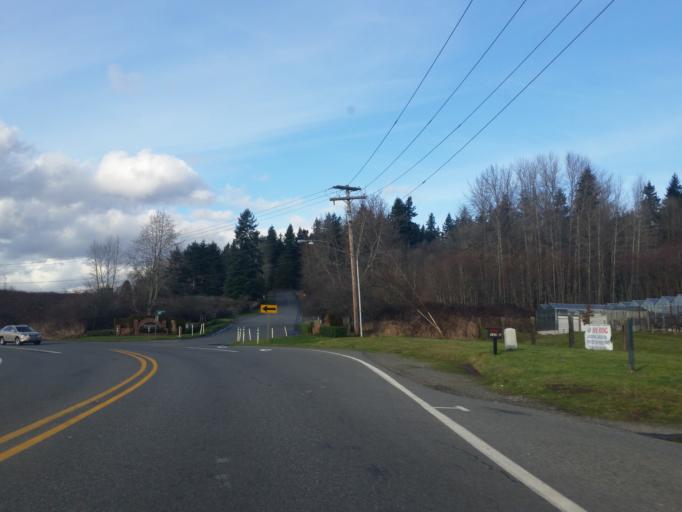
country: US
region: Washington
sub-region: King County
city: Redmond
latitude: 47.7142
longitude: -122.1317
